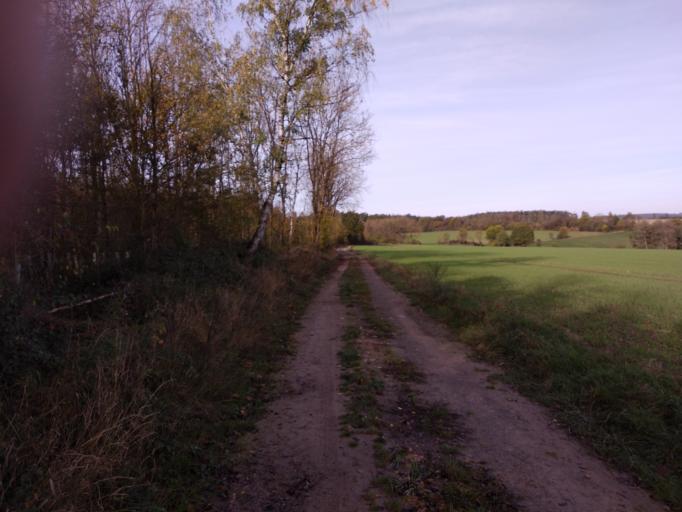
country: DE
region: North Rhine-Westphalia
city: Beverungen
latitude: 51.6795
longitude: 9.3583
